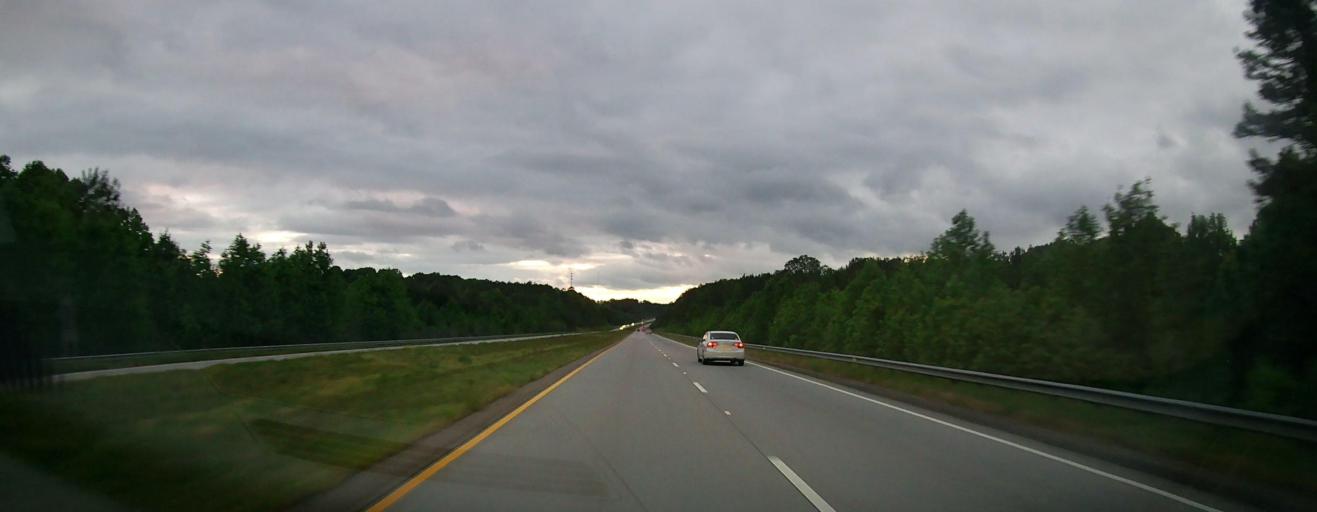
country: US
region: Georgia
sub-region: Jackson County
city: Jefferson
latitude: 34.0934
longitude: -83.5855
